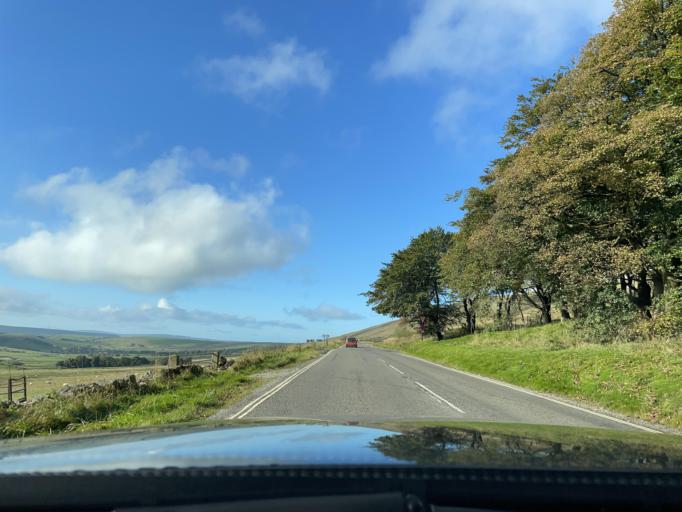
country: GB
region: England
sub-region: Derbyshire
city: High Peak
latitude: 53.3454
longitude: -1.8172
